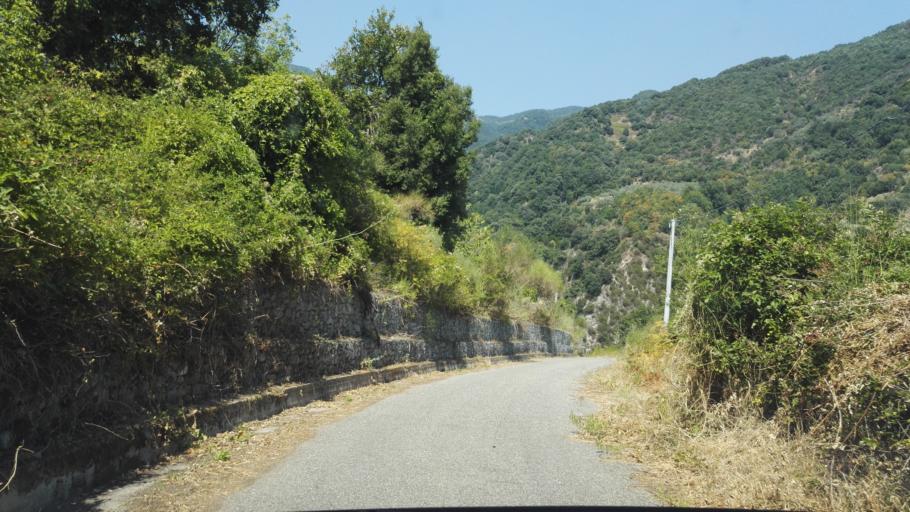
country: IT
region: Calabria
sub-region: Provincia di Reggio Calabria
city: Bivongi
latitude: 38.4905
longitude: 16.4193
